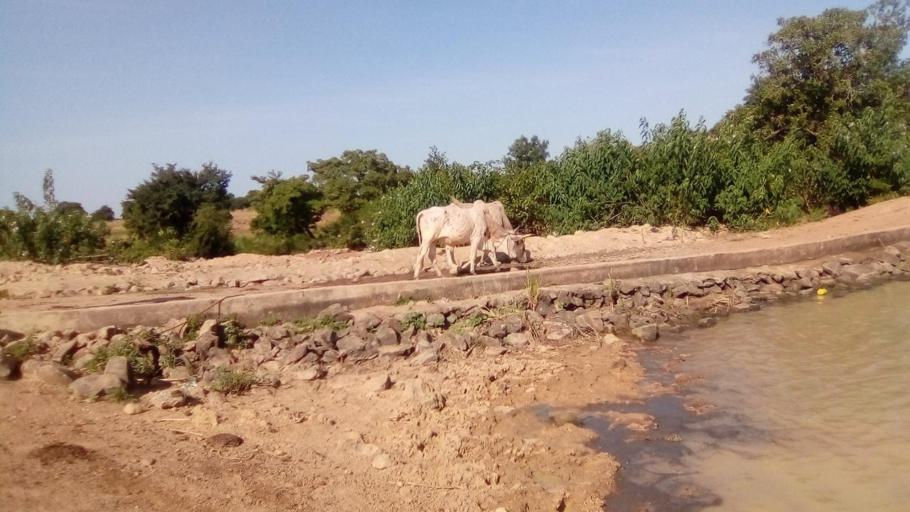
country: TG
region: Savanes
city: Dapaong
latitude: 11.0557
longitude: 0.1238
